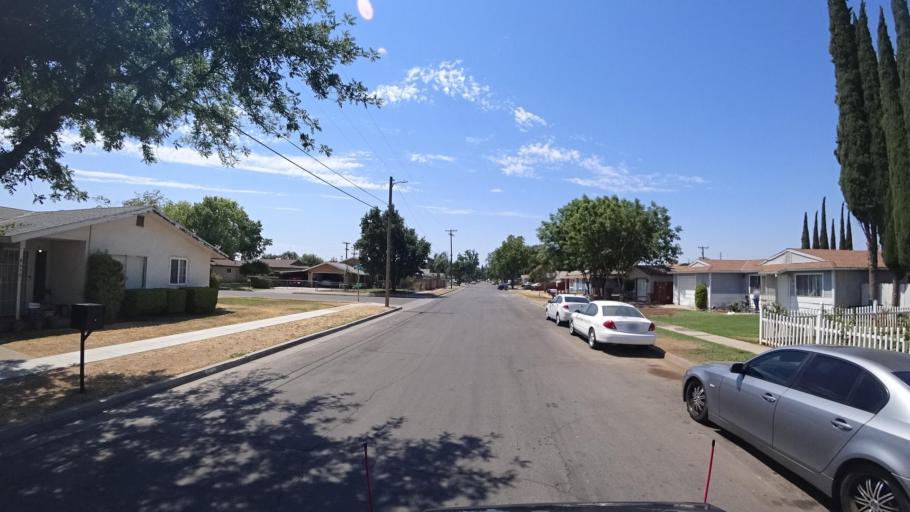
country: US
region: California
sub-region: Fresno County
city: Tarpey Village
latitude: 36.7836
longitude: -119.6861
